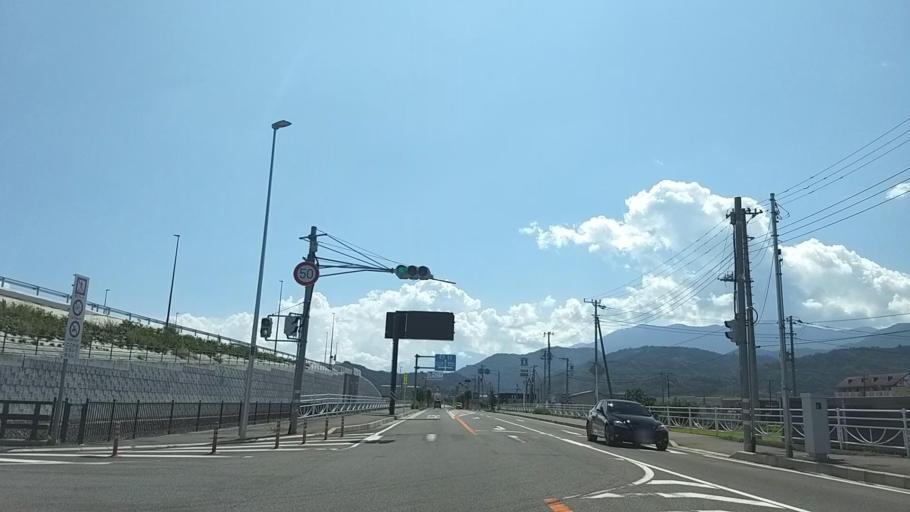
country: JP
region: Yamanashi
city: Ryuo
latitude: 35.5599
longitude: 138.4716
